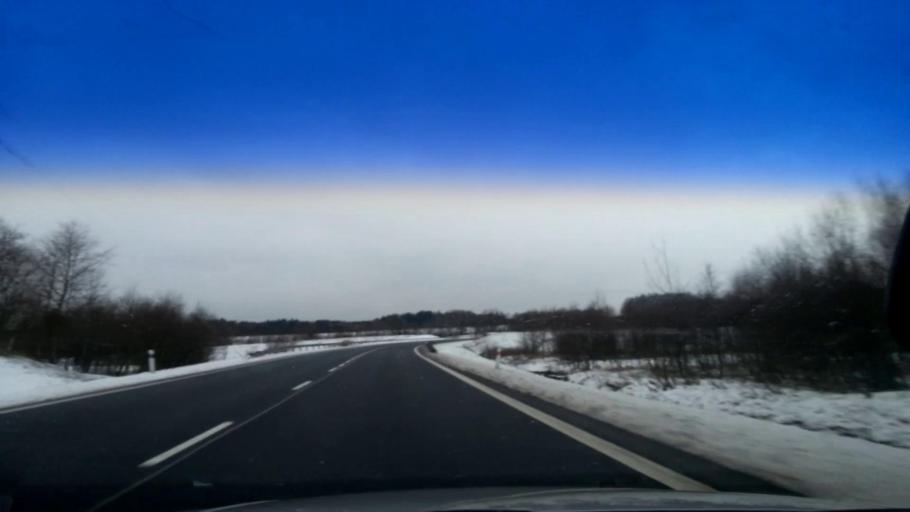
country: CZ
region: Karlovarsky
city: As
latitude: 50.1979
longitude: 12.2045
